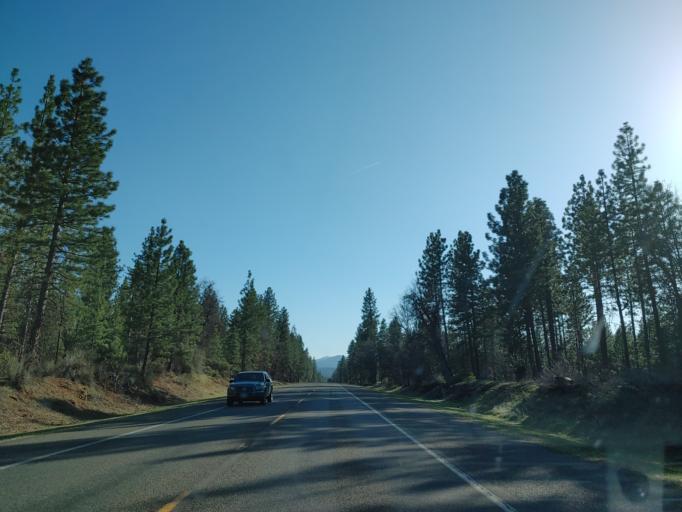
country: US
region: California
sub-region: Shasta County
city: Burney
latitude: 40.9056
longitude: -121.6384
